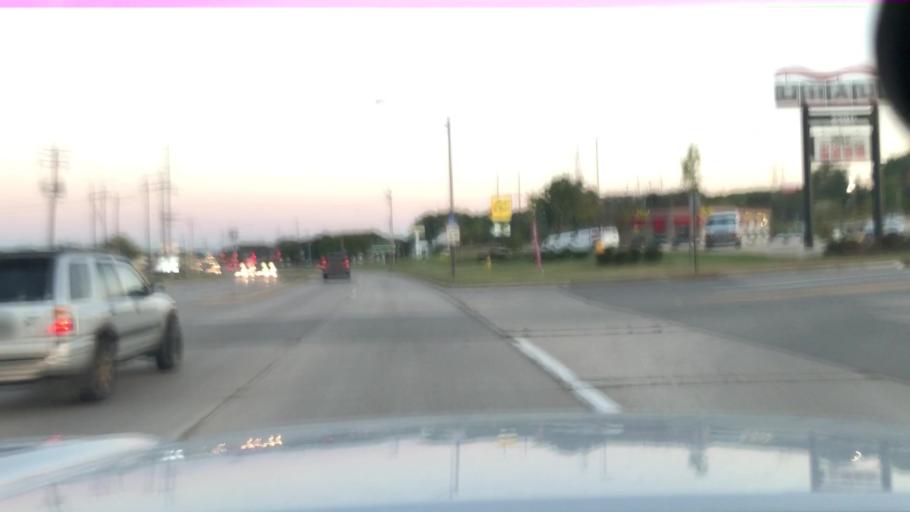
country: US
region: Wisconsin
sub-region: Brown County
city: Allouez
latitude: 44.4865
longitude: -87.9713
